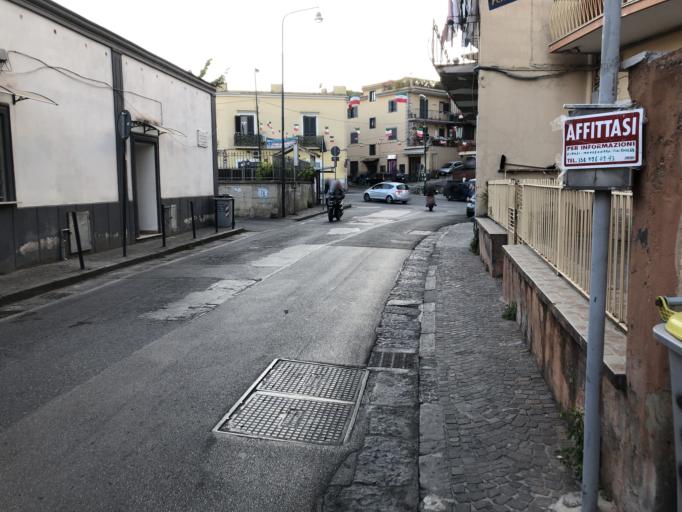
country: IT
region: Campania
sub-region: Provincia di Napoli
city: Torre Caracciolo
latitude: 40.8737
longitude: 14.2118
